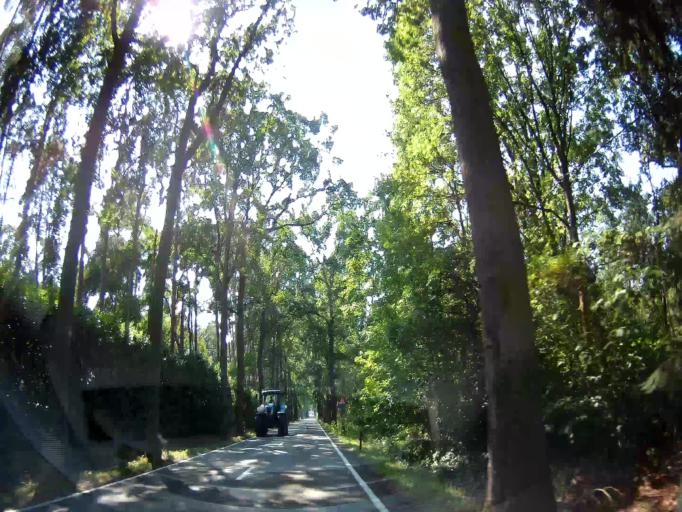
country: BE
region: Flanders
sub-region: Provincie Antwerpen
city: Dessel
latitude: 51.2793
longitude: 5.1596
